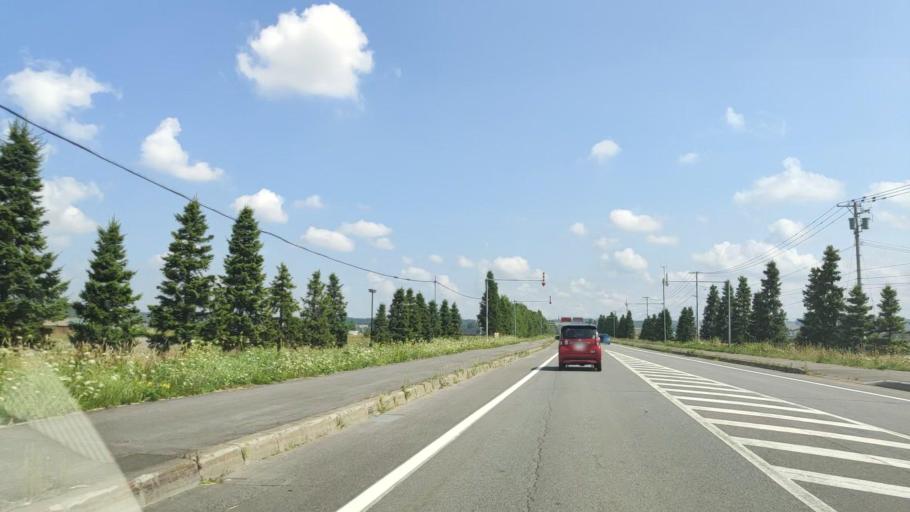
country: JP
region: Hokkaido
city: Shimo-furano
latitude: 43.4763
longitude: 142.4567
